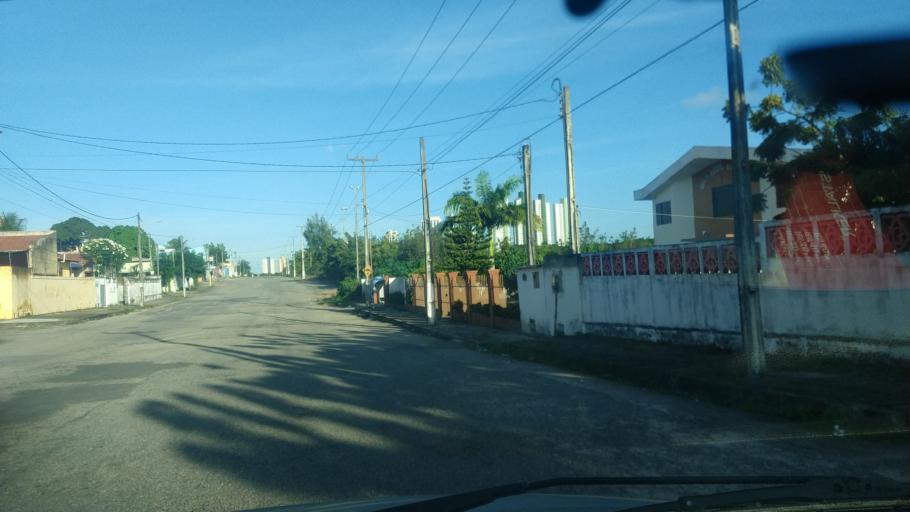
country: BR
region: Rio Grande do Norte
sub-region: Natal
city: Natal
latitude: -5.8734
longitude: -35.1885
